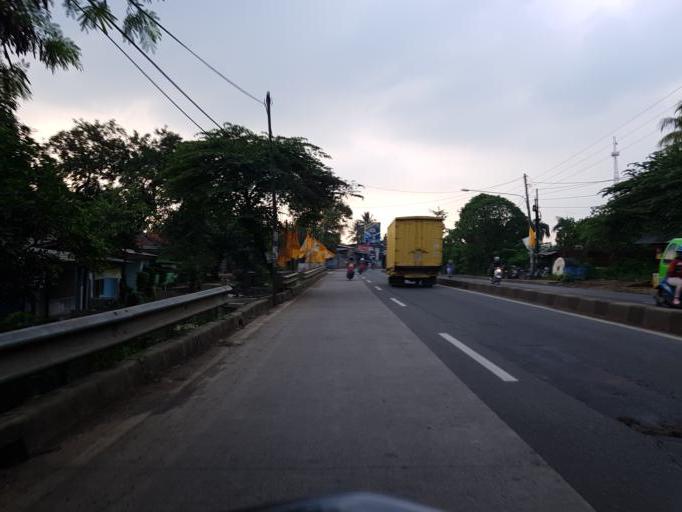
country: ID
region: West Java
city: Parung
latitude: -6.4844
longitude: 106.7339
